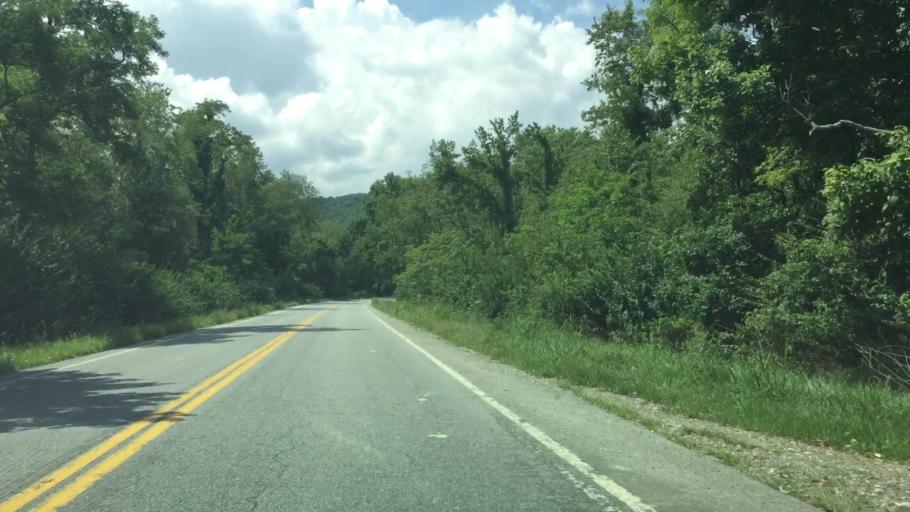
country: US
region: Virginia
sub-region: Pulaski County
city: Pulaski
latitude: 36.9999
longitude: -80.7962
